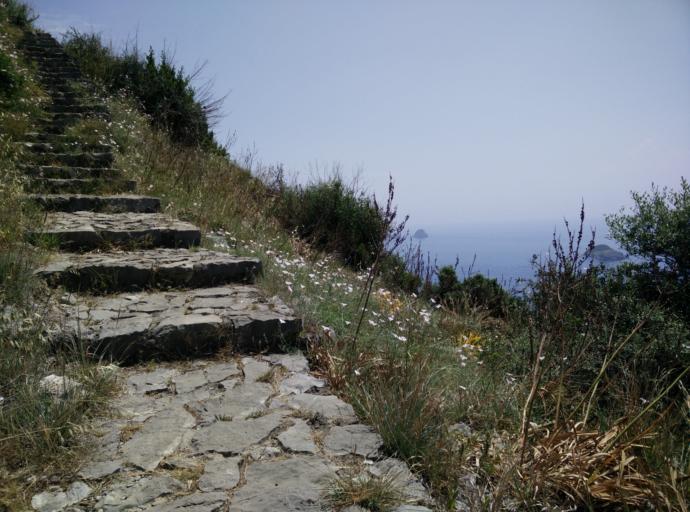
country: IT
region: Campania
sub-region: Provincia di Napoli
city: Massa Lubrense
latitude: 40.5935
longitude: 14.3792
